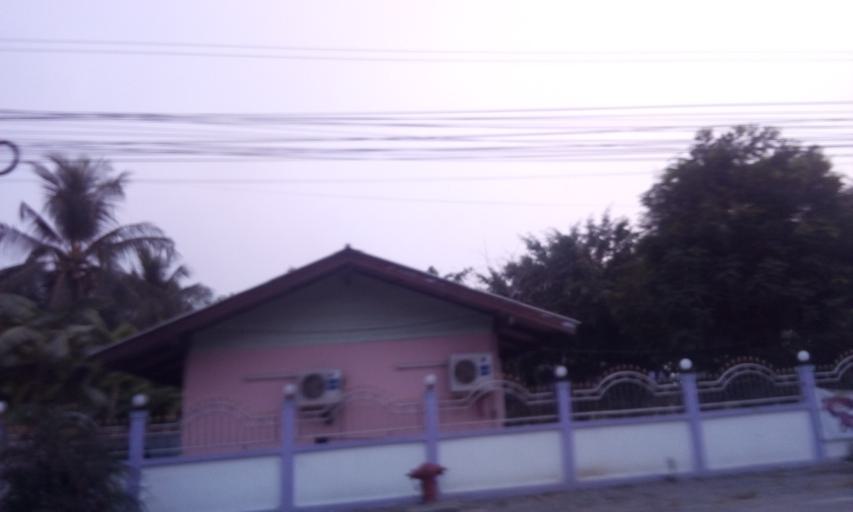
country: TH
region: Bangkok
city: Nong Chok
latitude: 13.8483
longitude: 100.8913
